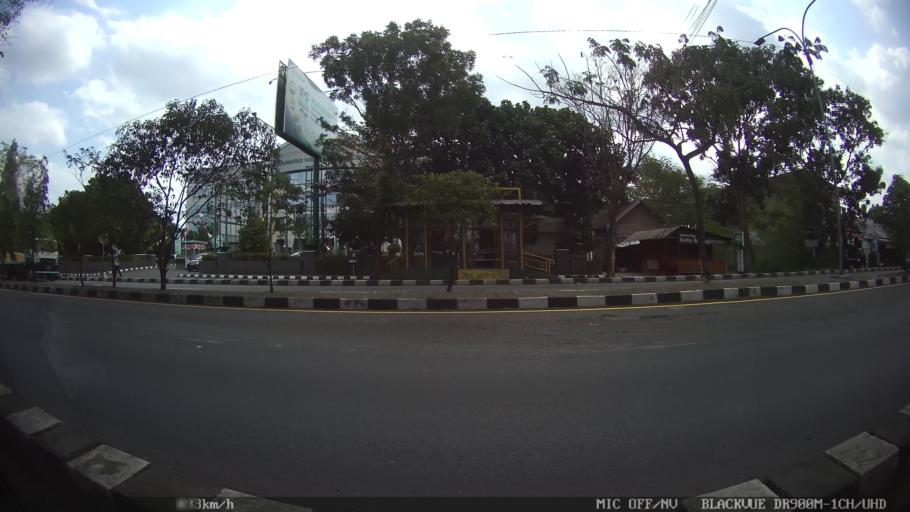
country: ID
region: Daerah Istimewa Yogyakarta
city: Gamping Lor
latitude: -7.7680
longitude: 110.3349
